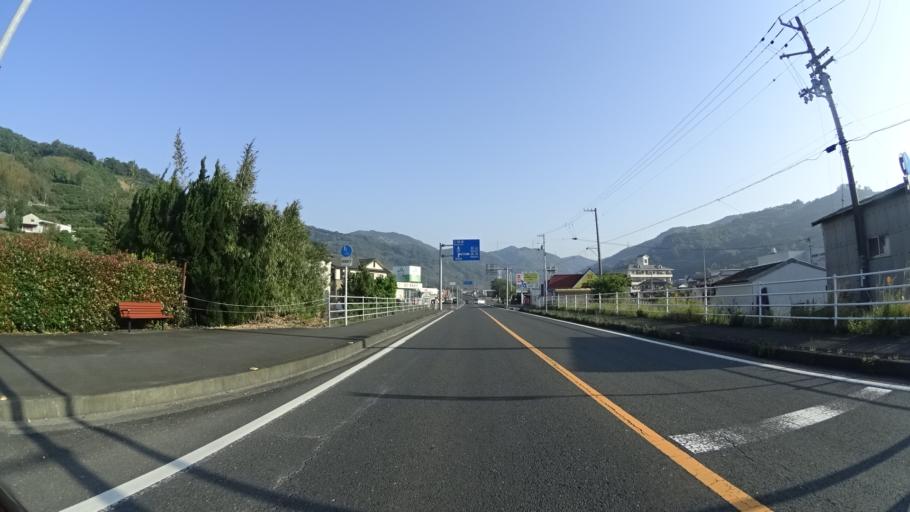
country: JP
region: Ehime
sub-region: Nishiuwa-gun
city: Ikata-cho
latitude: 33.4854
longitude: 132.3990
